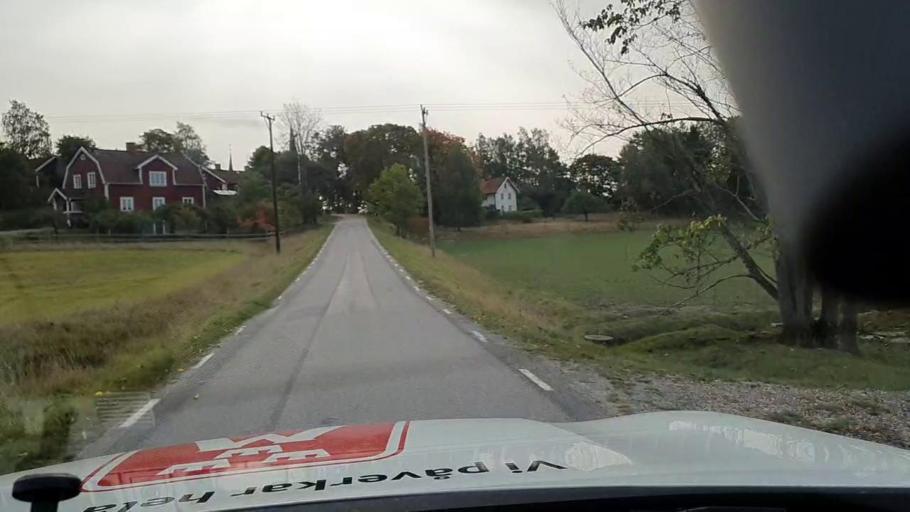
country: SE
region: Soedermanland
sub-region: Nykopings Kommun
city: Stigtomta
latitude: 58.9835
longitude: 16.9294
